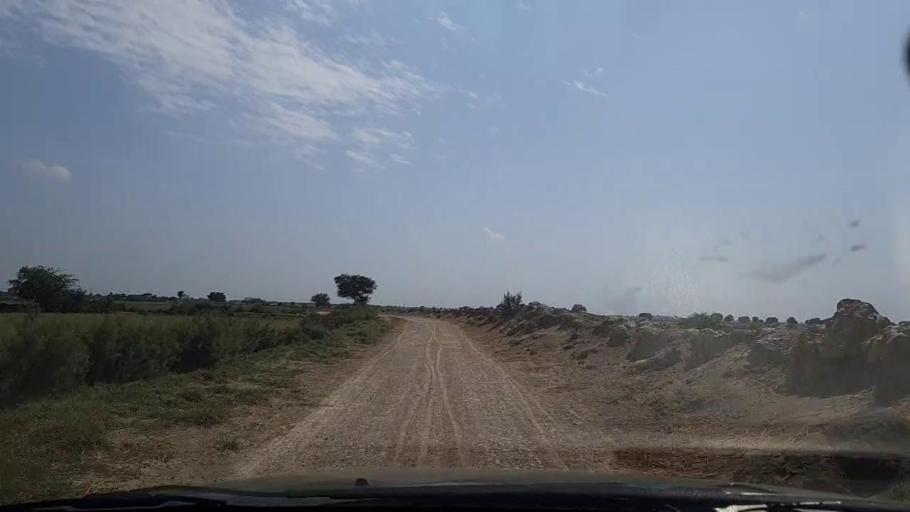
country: PK
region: Sindh
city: Mirpur Batoro
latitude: 24.5815
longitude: 68.1956
